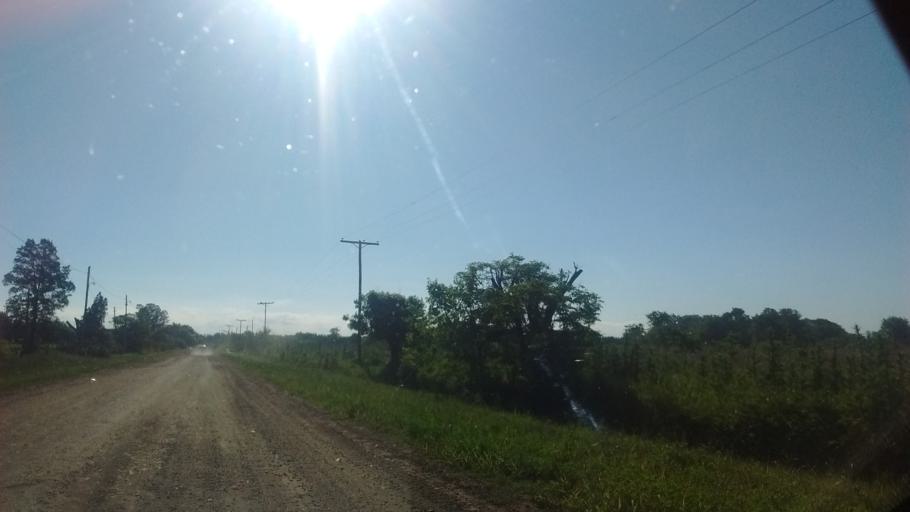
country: AR
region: Santa Fe
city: Funes
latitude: -32.8608
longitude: -60.7982
